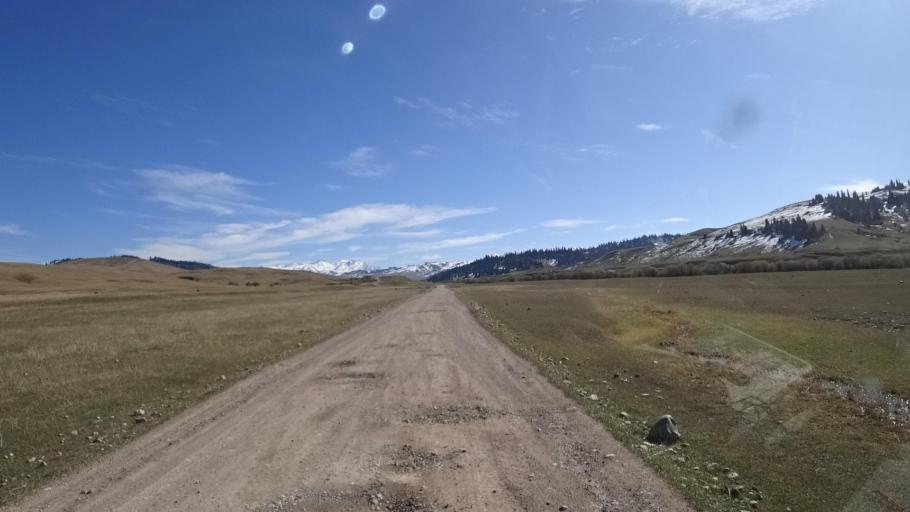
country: KZ
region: Almaty Oblysy
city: Kegen
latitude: 42.7403
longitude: 79.0048
